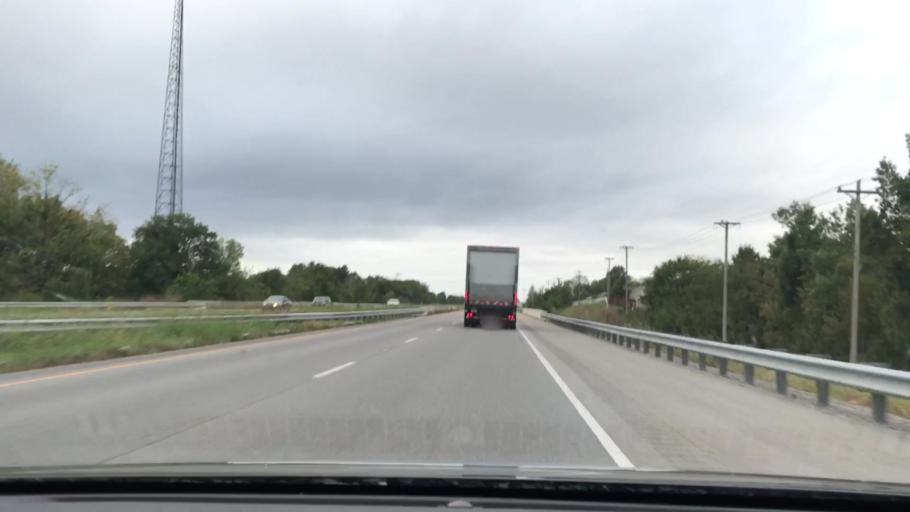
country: US
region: Kentucky
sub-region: Christian County
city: Hopkinsville
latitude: 36.8185
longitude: -87.4883
